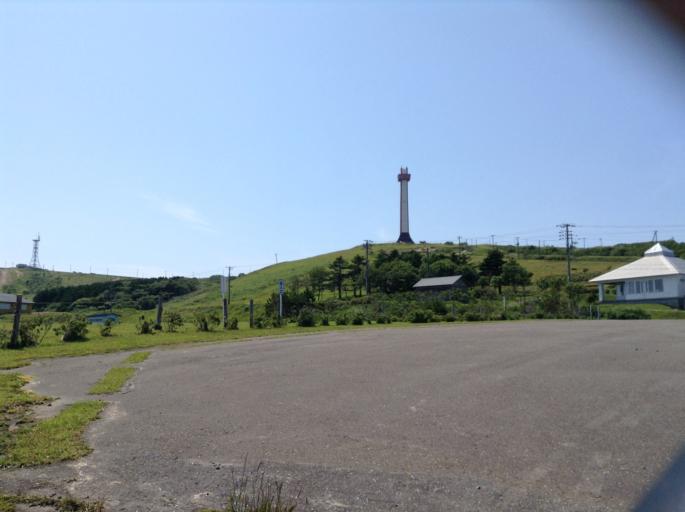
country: JP
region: Hokkaido
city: Wakkanai
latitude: 45.4182
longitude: 141.6704
